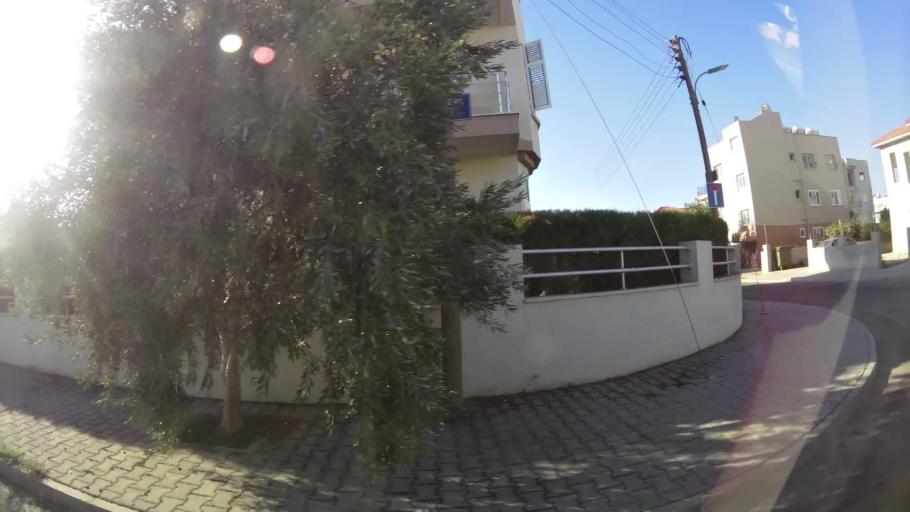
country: CY
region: Lefkosia
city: Nicosia
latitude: 35.2137
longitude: 33.2947
